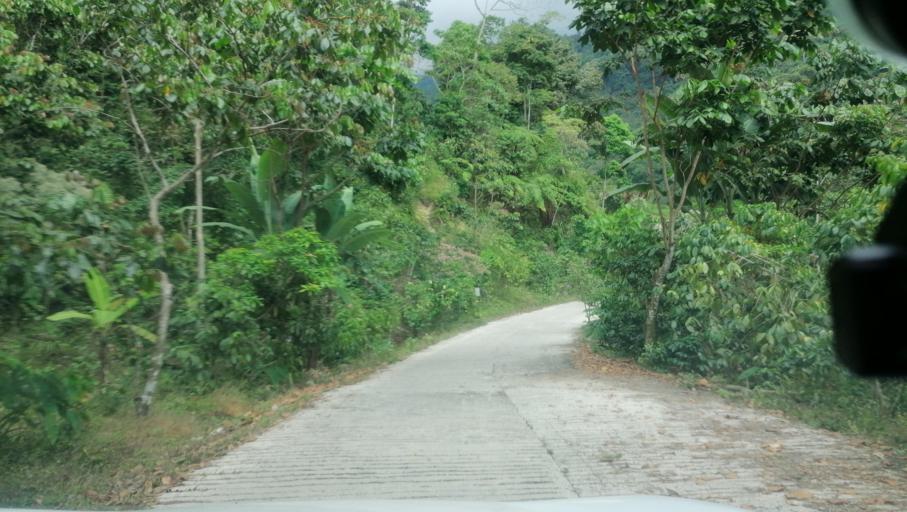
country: MX
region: Chiapas
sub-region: Cacahoatan
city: Benito Juarez
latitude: 15.1020
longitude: -92.1876
